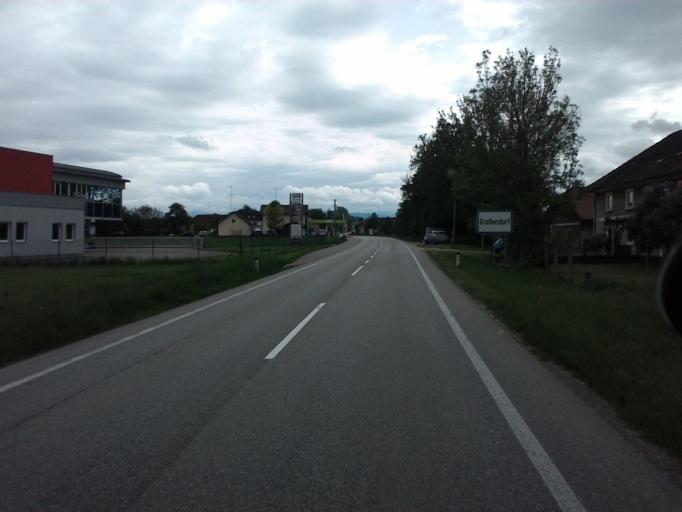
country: AT
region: Upper Austria
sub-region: Wels-Land
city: Sattledt
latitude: 48.0404
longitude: 14.0584
